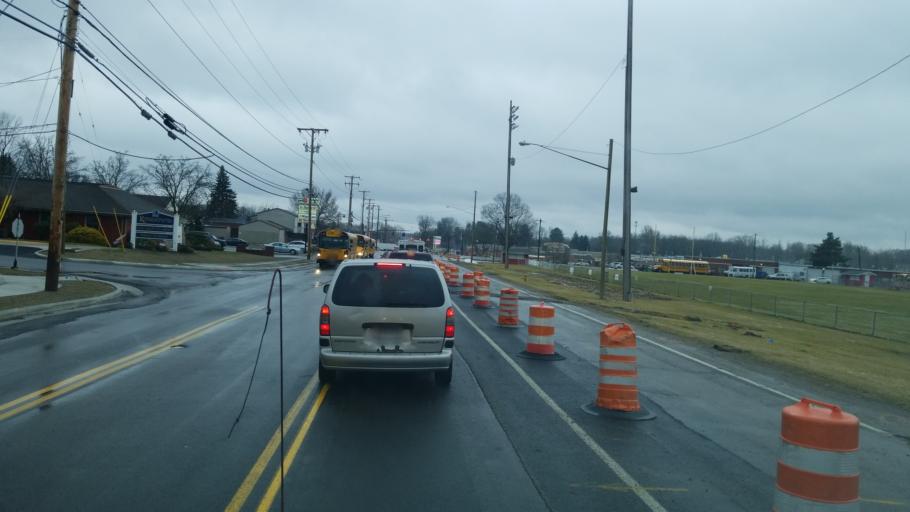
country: US
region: Ohio
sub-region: Summit County
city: Norton
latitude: 41.0283
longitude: -81.6382
